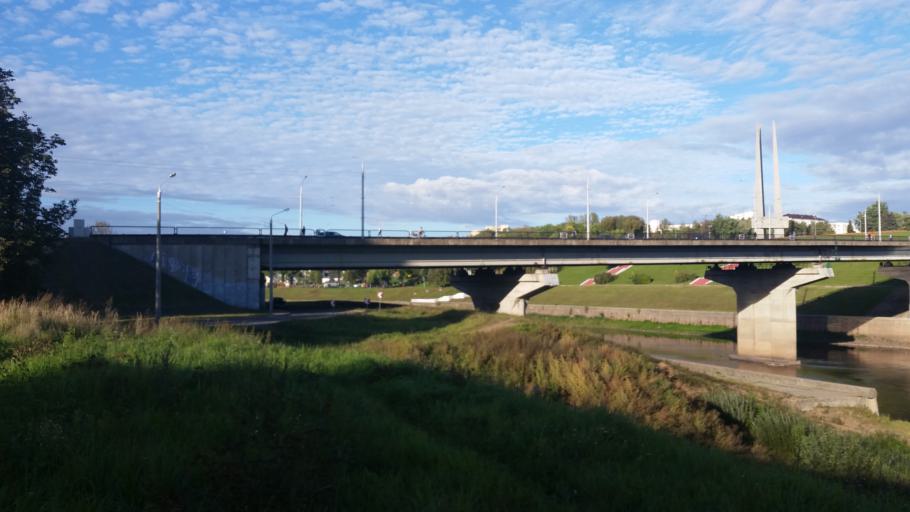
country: BY
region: Vitebsk
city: Vitebsk
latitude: 55.1833
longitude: 30.1949
